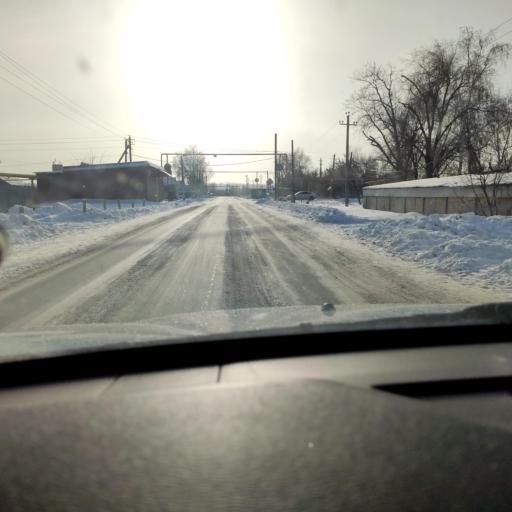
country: RU
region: Samara
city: Smyshlyayevka
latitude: 53.1630
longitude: 50.3829
